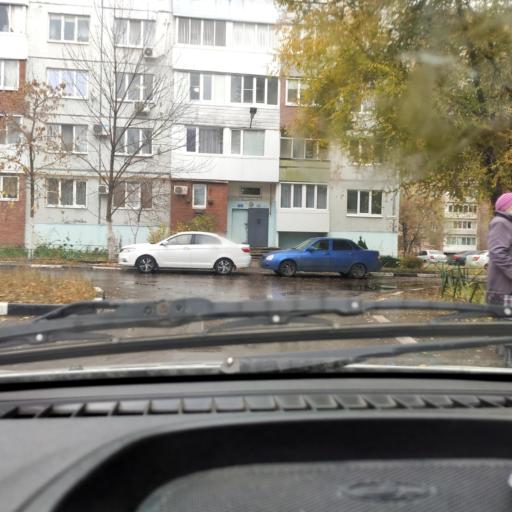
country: RU
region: Samara
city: Zhigulevsk
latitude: 53.4776
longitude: 49.4836
